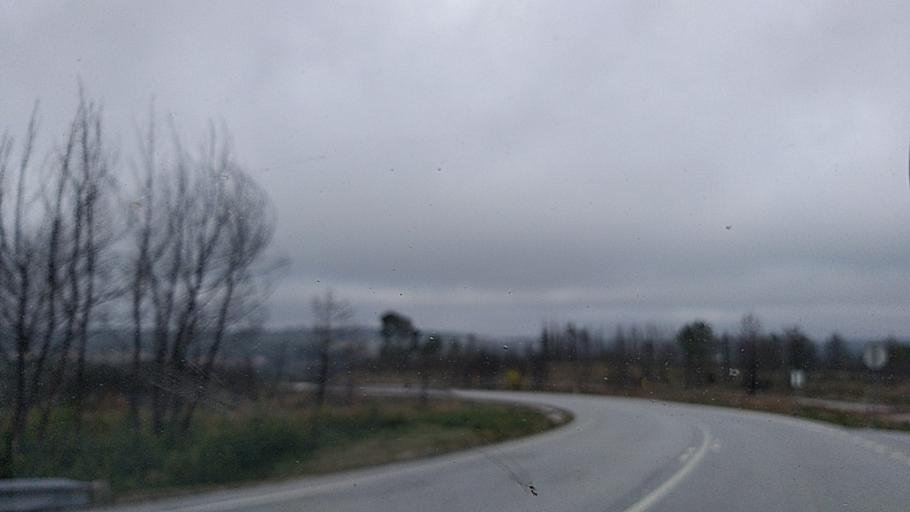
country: PT
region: Guarda
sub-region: Fornos de Algodres
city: Fornos de Algodres
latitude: 40.7066
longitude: -7.4828
